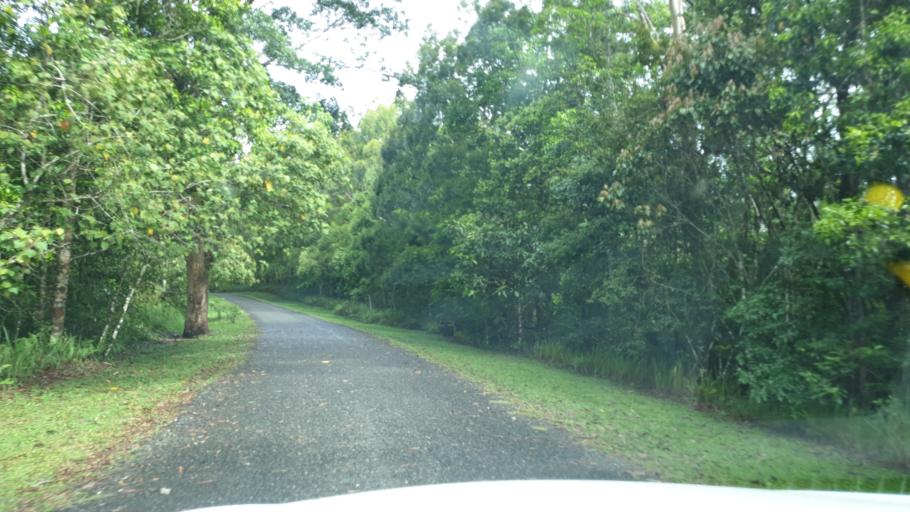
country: PG
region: National Capital
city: Port Moresby
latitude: -9.4339
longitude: 147.3726
